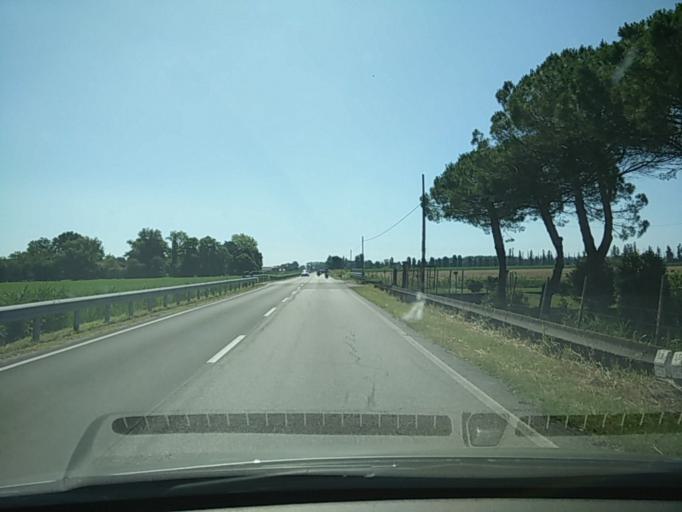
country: IT
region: Veneto
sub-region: Provincia di Venezia
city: San Giorgio di Livenza
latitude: 45.6239
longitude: 12.7922
